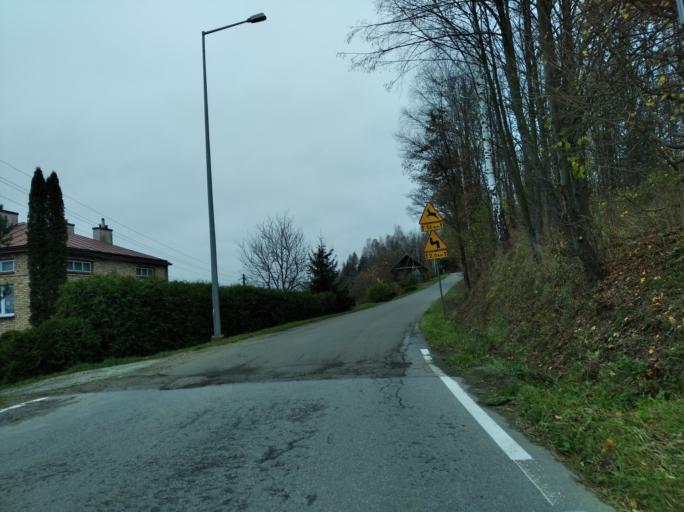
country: PL
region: Subcarpathian Voivodeship
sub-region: Powiat krosnienski
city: Leki
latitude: 49.8271
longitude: 21.6379
